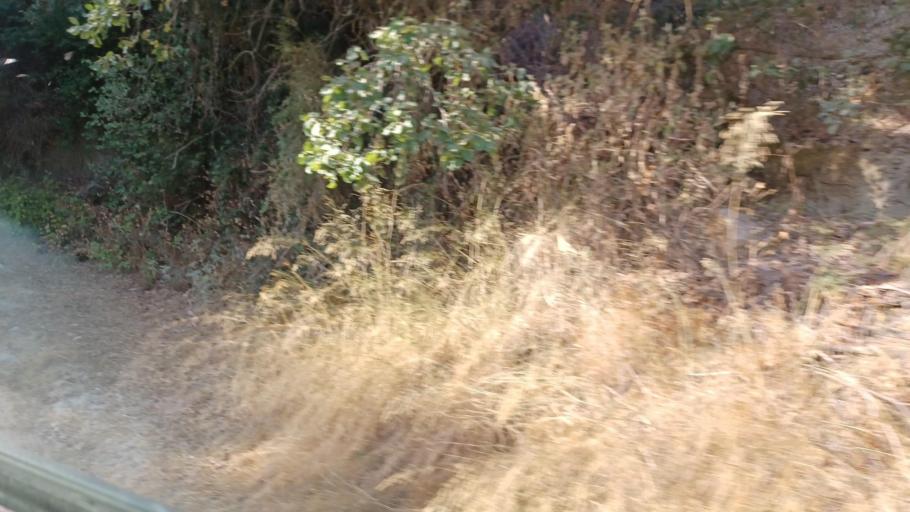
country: CY
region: Pafos
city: Tala
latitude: 34.9284
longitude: 32.4882
